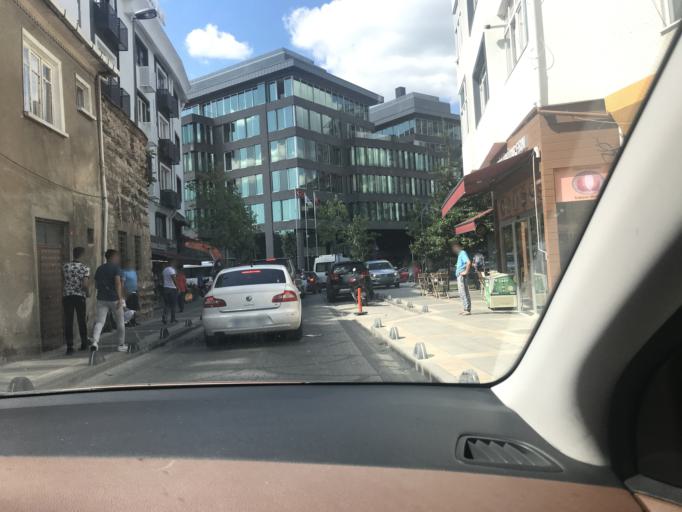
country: TR
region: Istanbul
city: UEskuedar
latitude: 41.0196
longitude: 29.0199
